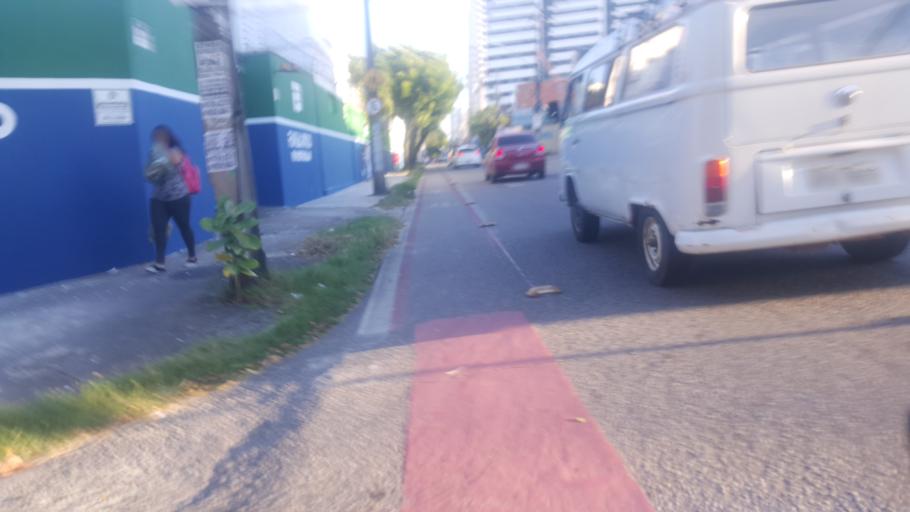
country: BR
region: Ceara
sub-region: Fortaleza
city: Fortaleza
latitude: -3.7383
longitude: -38.5331
